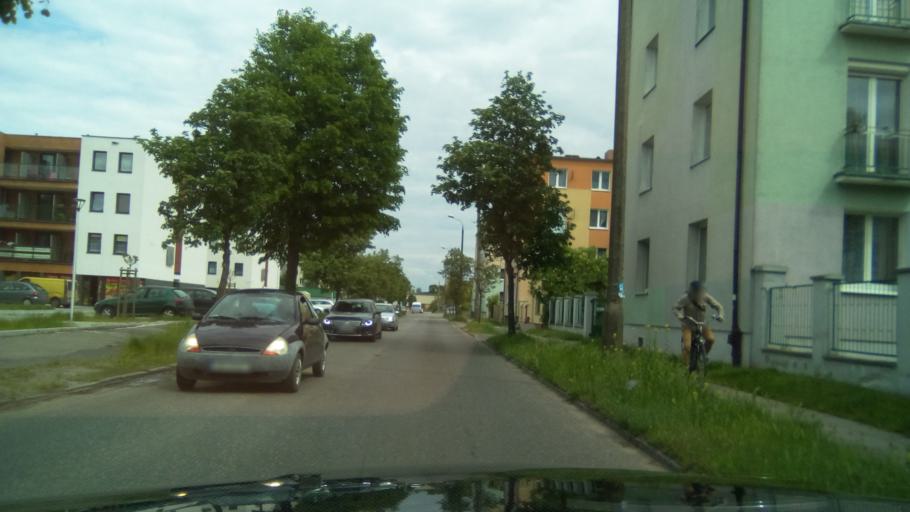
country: PL
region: Greater Poland Voivodeship
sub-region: Powiat gnieznienski
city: Gniezno
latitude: 52.5185
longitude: 17.5974
